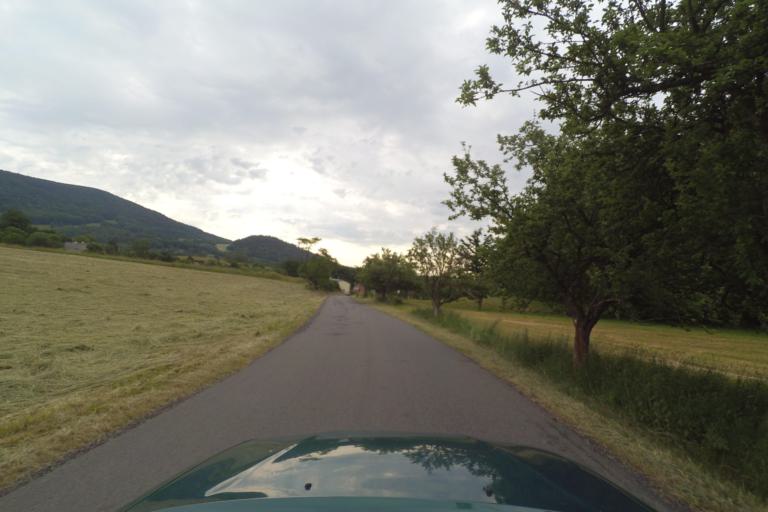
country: CZ
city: Cesky Dub
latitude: 50.7032
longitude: 14.9857
